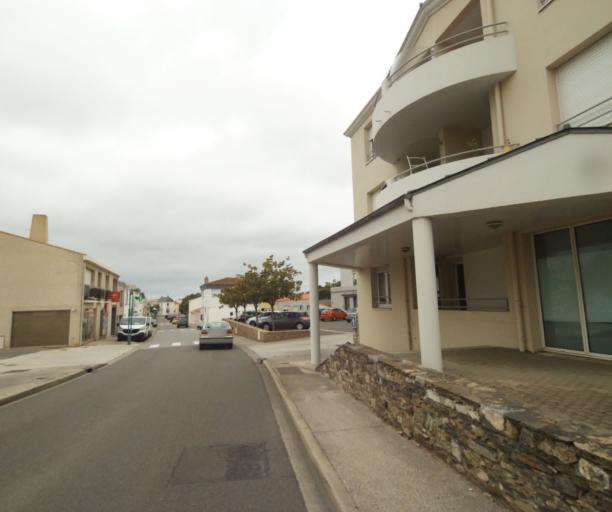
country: FR
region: Pays de la Loire
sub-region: Departement de la Vendee
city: Chateau-d'Olonne
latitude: 46.5043
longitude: -1.7359
